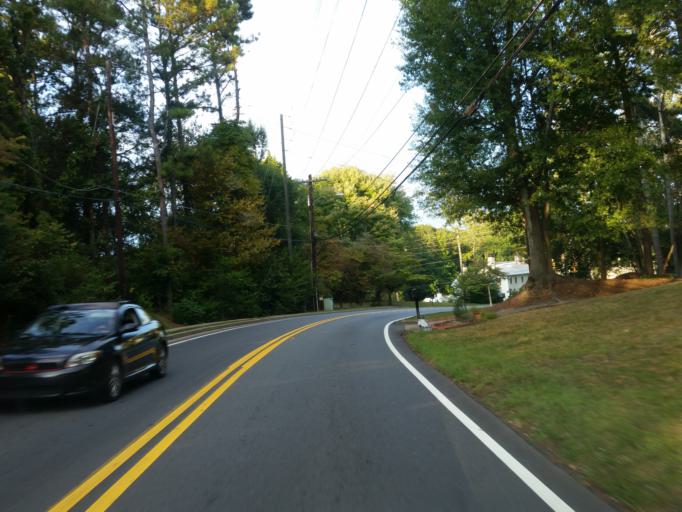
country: US
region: Georgia
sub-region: Cobb County
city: Marietta
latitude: 33.9846
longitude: -84.4601
